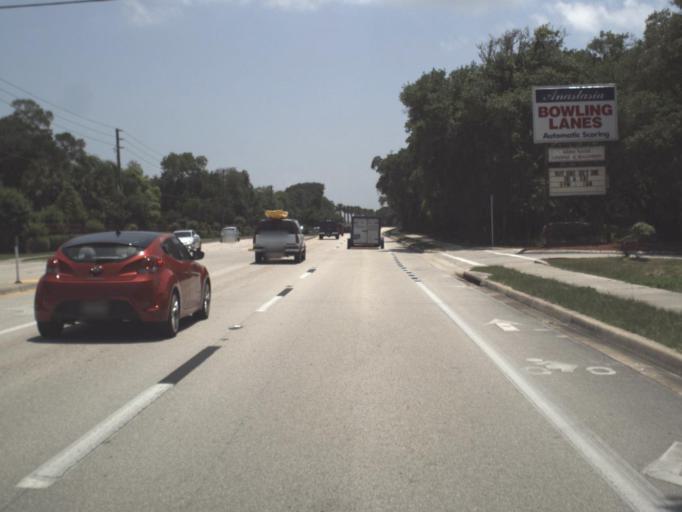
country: US
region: Florida
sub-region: Saint Johns County
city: Saint Augustine Beach
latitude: 29.8375
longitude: -81.2754
